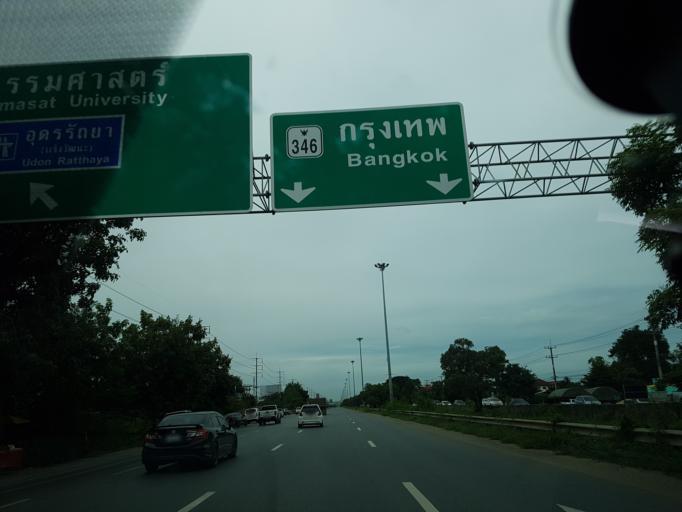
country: TH
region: Pathum Thani
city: Sam Khok
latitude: 14.0805
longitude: 100.5709
